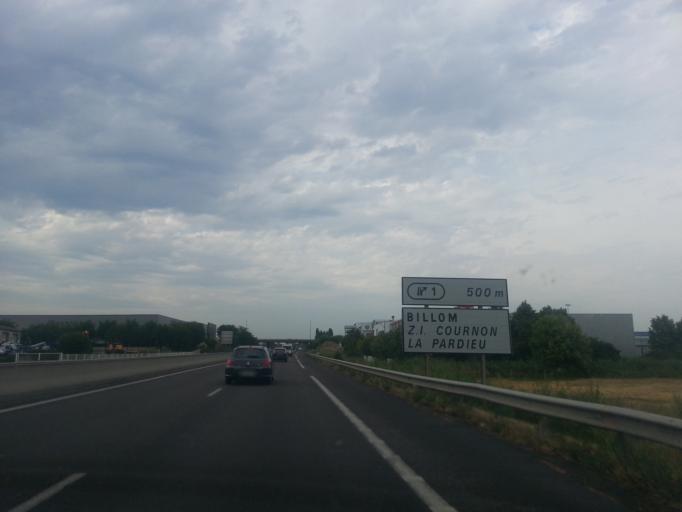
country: FR
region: Auvergne
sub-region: Departement du Puy-de-Dome
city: Perignat-les-Sarlieve
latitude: 45.7515
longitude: 3.1433
